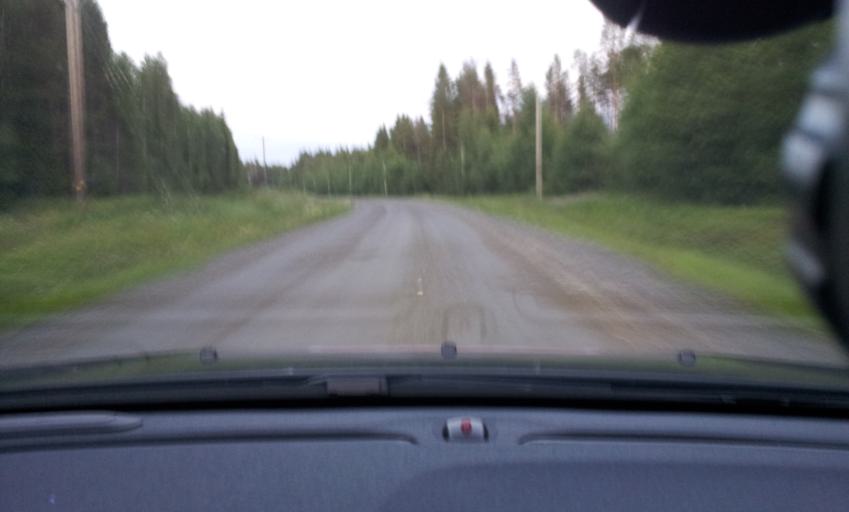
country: SE
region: Jaemtland
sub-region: Ragunda Kommun
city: Hammarstrand
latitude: 62.9419
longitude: 16.1118
